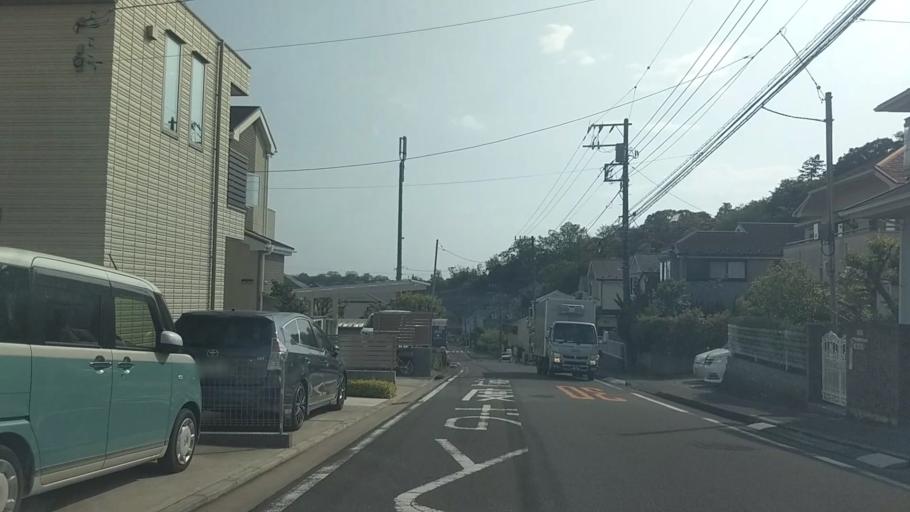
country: JP
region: Kanagawa
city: Kamakura
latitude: 35.3766
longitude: 139.5557
